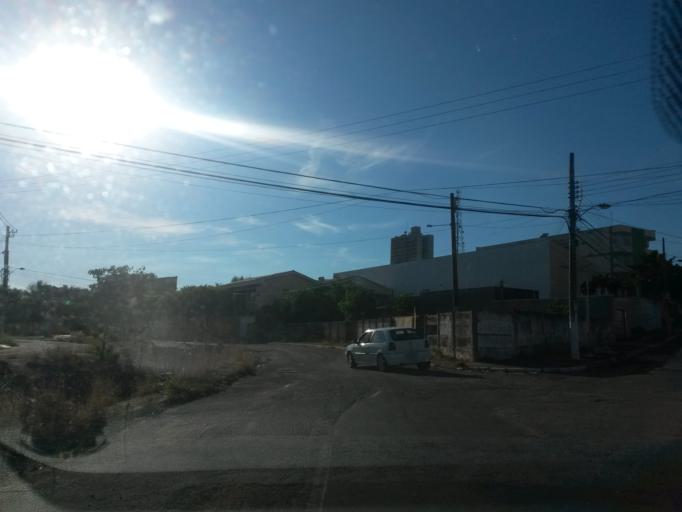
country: BR
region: Mato Grosso
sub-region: Cuiaba
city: Cuiaba
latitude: -15.6021
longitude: -56.0821
